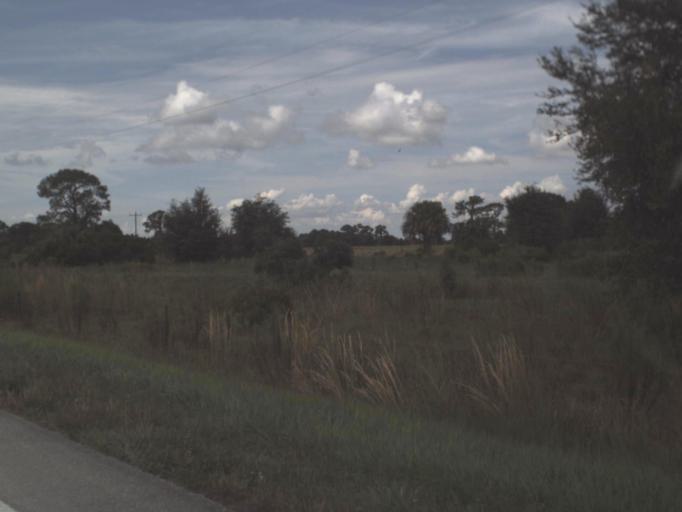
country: US
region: Florida
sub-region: Highlands County
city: Placid Lakes
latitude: 27.2089
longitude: -81.4706
